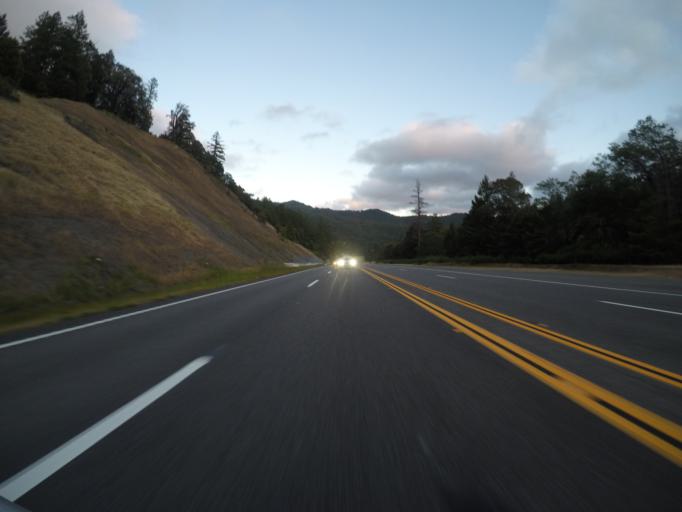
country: US
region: California
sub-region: Humboldt County
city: Redway
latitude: 40.0439
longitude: -123.7813
